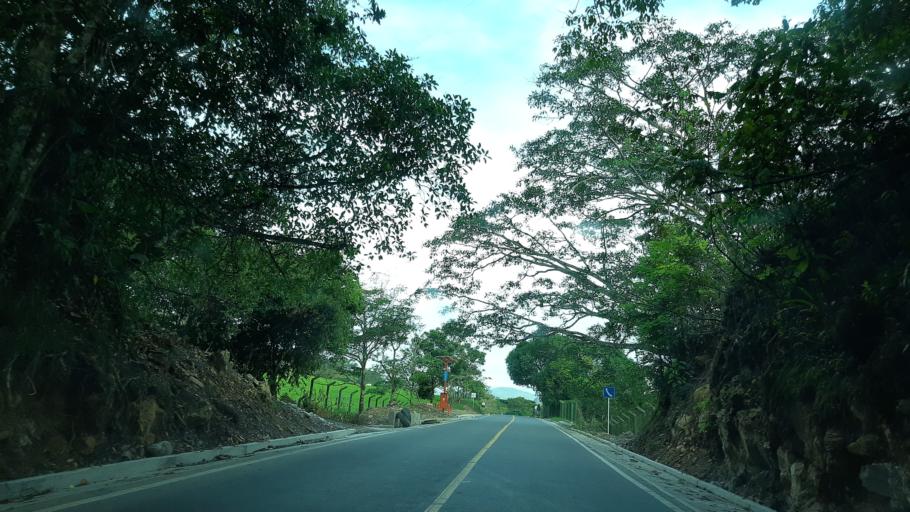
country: CO
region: Boyaca
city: San Luis de Gaceno
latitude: 4.8282
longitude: -73.2048
